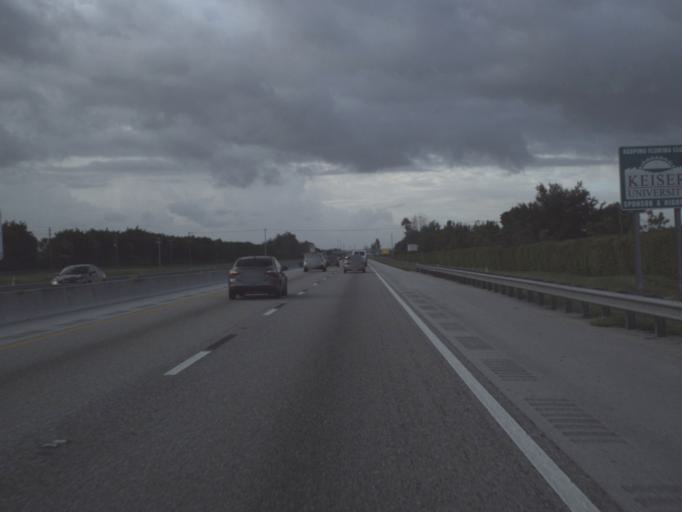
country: US
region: Florida
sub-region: Palm Beach County
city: Greenacres City
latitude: 26.5842
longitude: -80.1734
